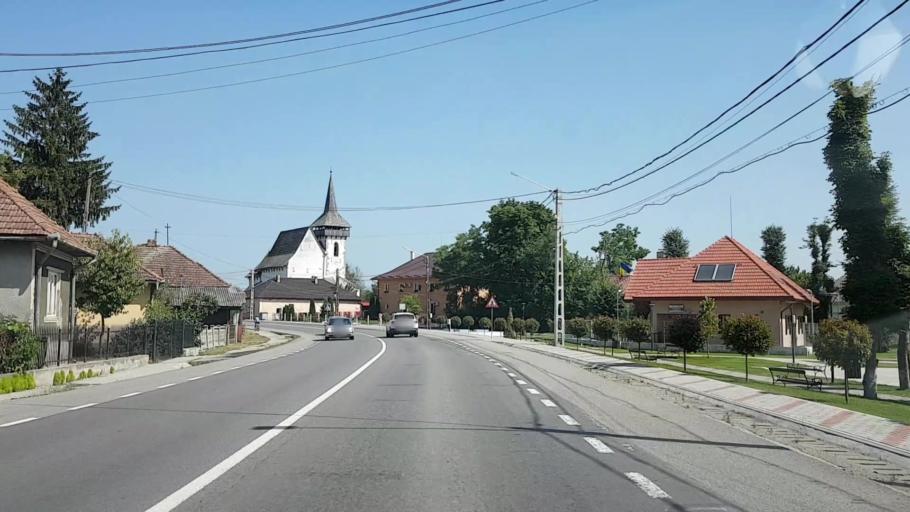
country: RO
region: Bistrita-Nasaud
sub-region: Comuna Sintereag
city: Sintereag
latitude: 47.1808
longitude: 24.2866
